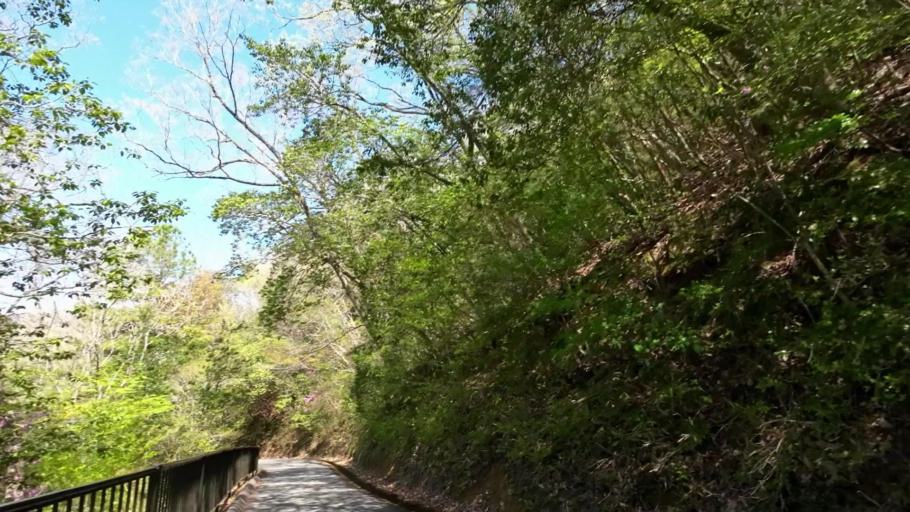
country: JP
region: Hyogo
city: Toyooka
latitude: 35.2981
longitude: 134.8284
